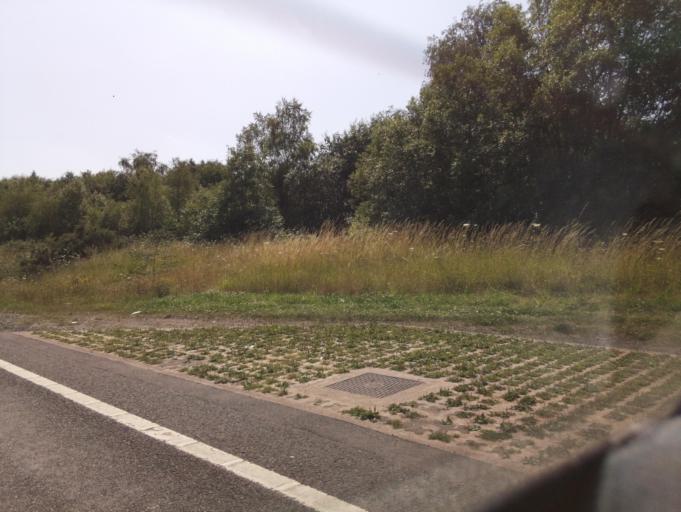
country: GB
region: Wales
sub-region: Caerphilly County Borough
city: Bargoed
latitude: 51.6783
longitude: -3.2230
